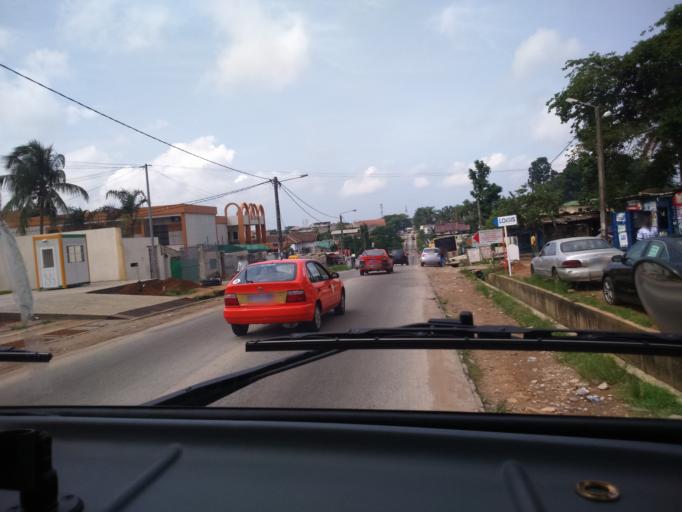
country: CI
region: Lagunes
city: Abidjan
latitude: 5.3622
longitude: -3.9789
